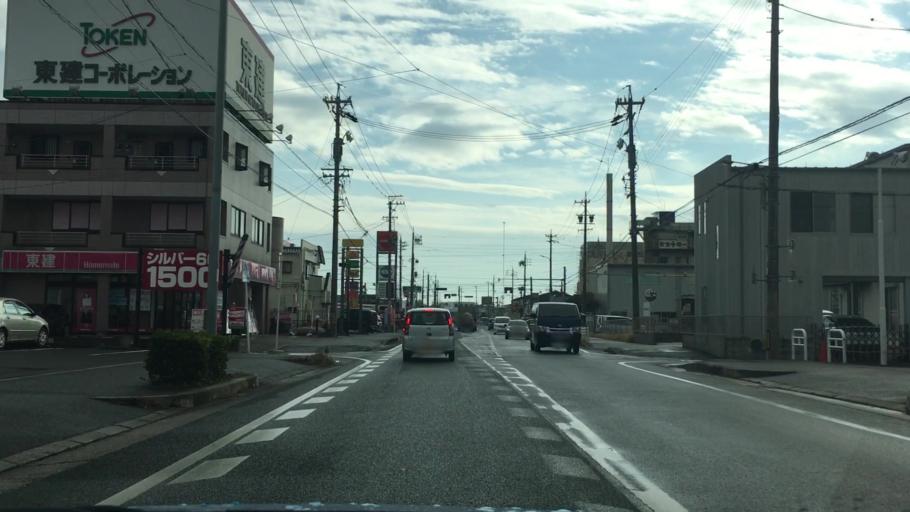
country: JP
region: Aichi
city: Toyohashi
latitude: 34.7677
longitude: 137.3636
